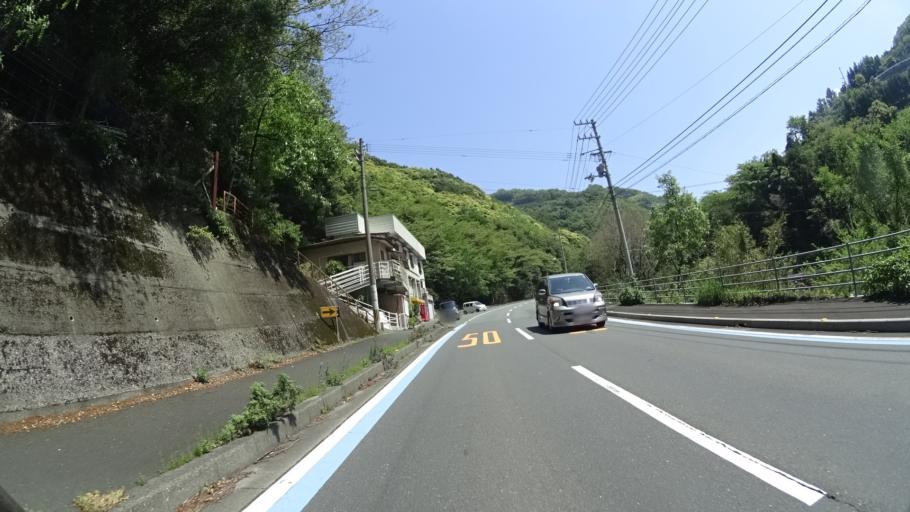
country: JP
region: Ehime
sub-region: Nishiuwa-gun
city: Ikata-cho
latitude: 33.4964
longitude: 132.3681
